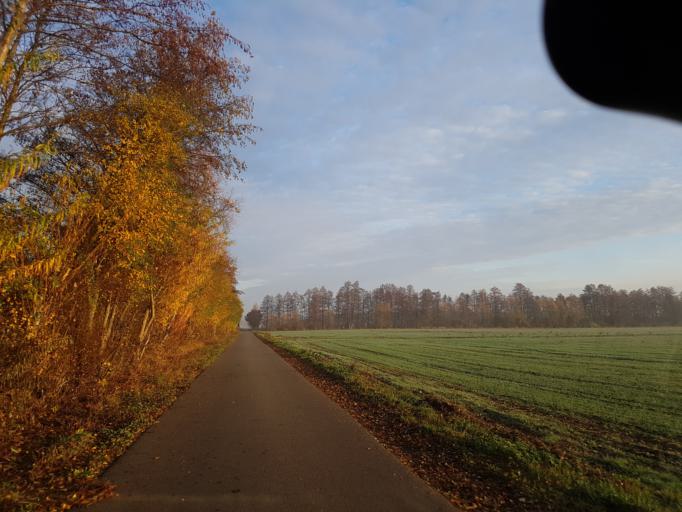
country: DE
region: Saxony-Anhalt
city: Elster
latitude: 51.8684
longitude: 12.8466
